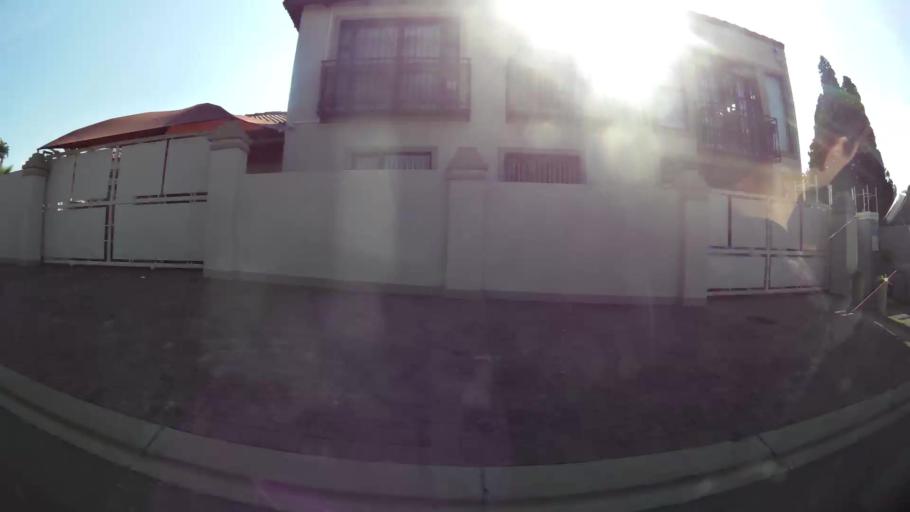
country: ZA
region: Gauteng
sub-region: City of Johannesburg Metropolitan Municipality
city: Johannesburg
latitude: -26.0886
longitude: 28.0229
